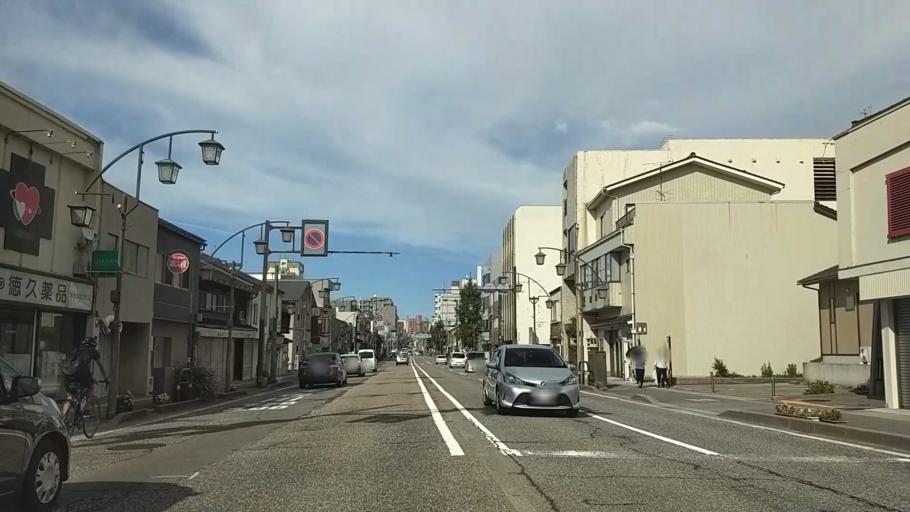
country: JP
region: Ishikawa
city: Nonoichi
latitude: 36.5518
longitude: 136.6454
